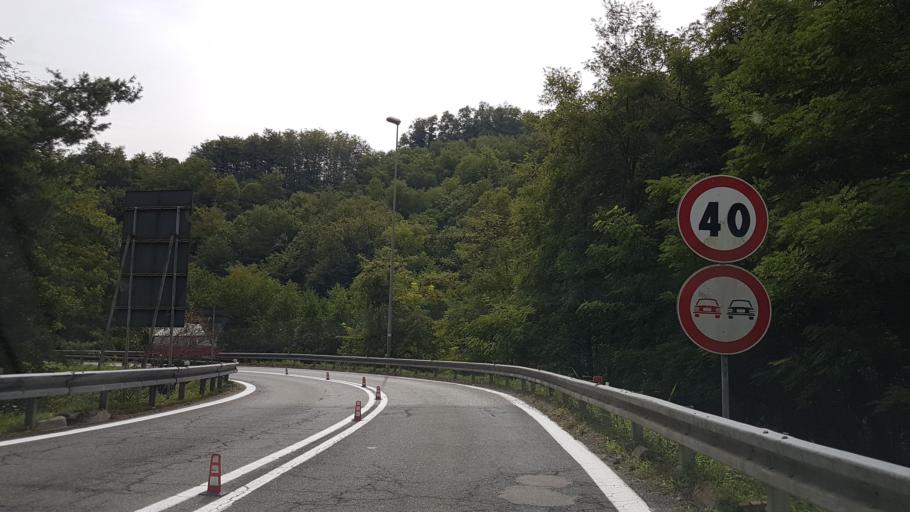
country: IT
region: Liguria
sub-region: Provincia di La Spezia
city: Carrodano
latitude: 44.2380
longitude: 9.6483
